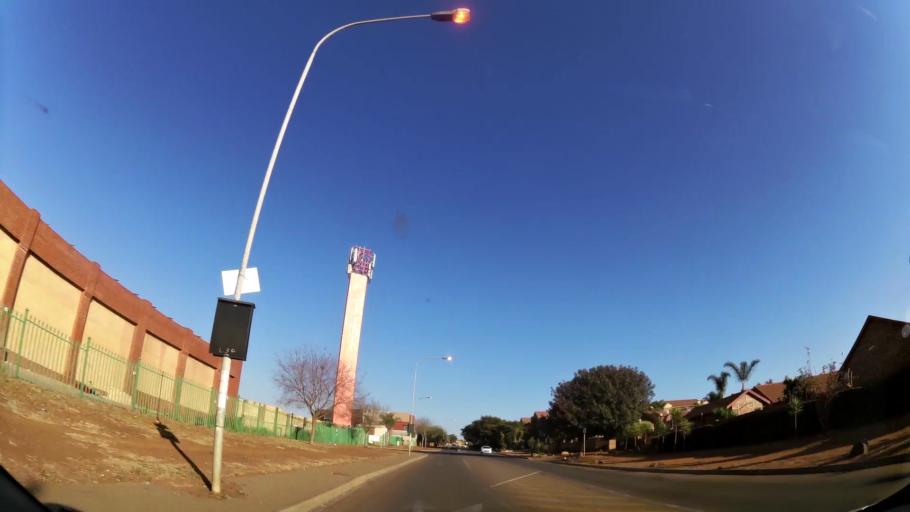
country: ZA
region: Gauteng
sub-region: City of Tshwane Metropolitan Municipality
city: Centurion
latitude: -25.8716
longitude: 28.1353
